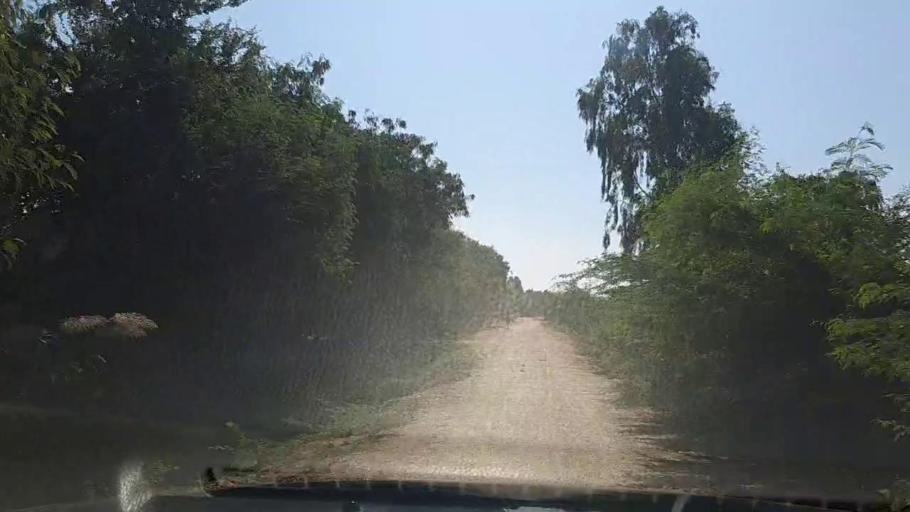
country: PK
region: Sindh
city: Thatta
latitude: 24.5928
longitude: 67.8197
